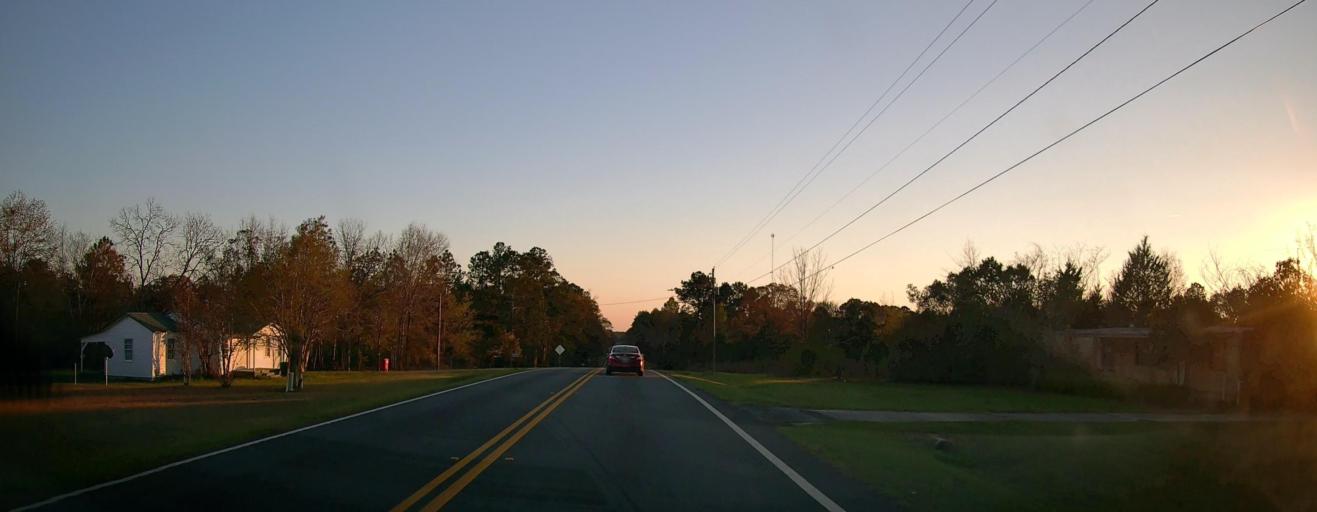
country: US
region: Georgia
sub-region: Dodge County
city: Chester
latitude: 32.3358
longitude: -83.0448
